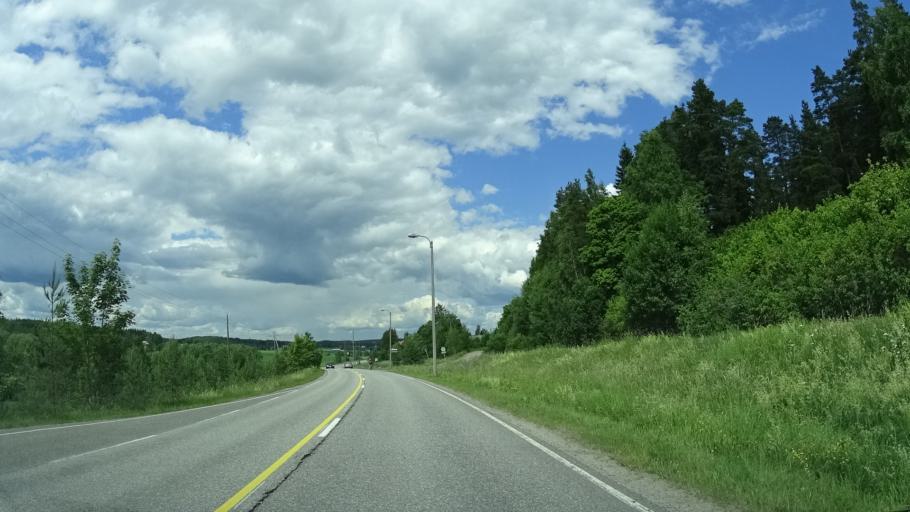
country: FI
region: Uusimaa
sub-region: Helsinki
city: Nurmijaervi
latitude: 60.3871
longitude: 24.6468
